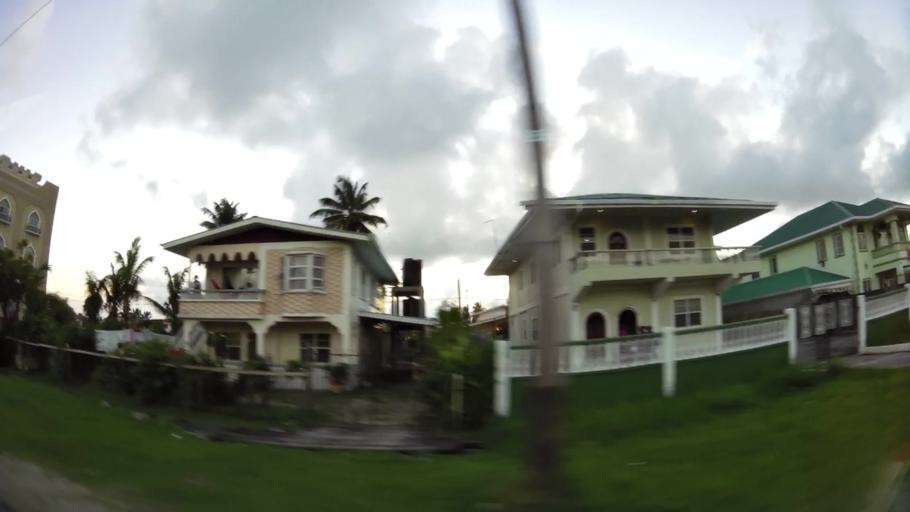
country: GY
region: Demerara-Mahaica
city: Georgetown
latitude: 6.8157
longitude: -58.0989
